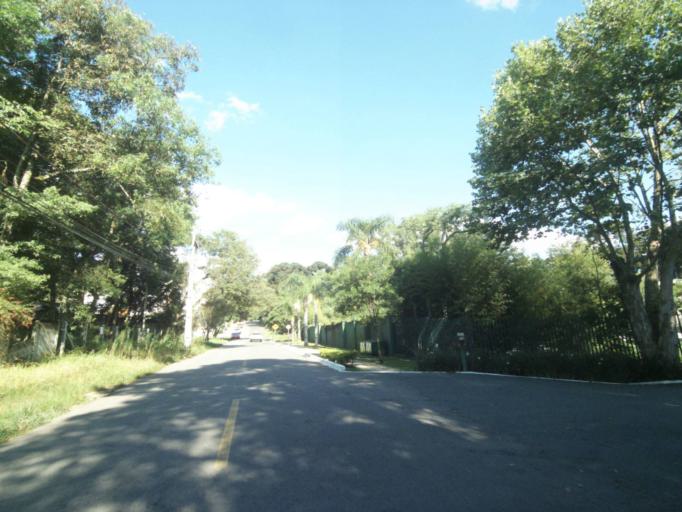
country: BR
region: Parana
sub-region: Curitiba
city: Curitiba
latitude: -25.4451
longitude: -49.3233
